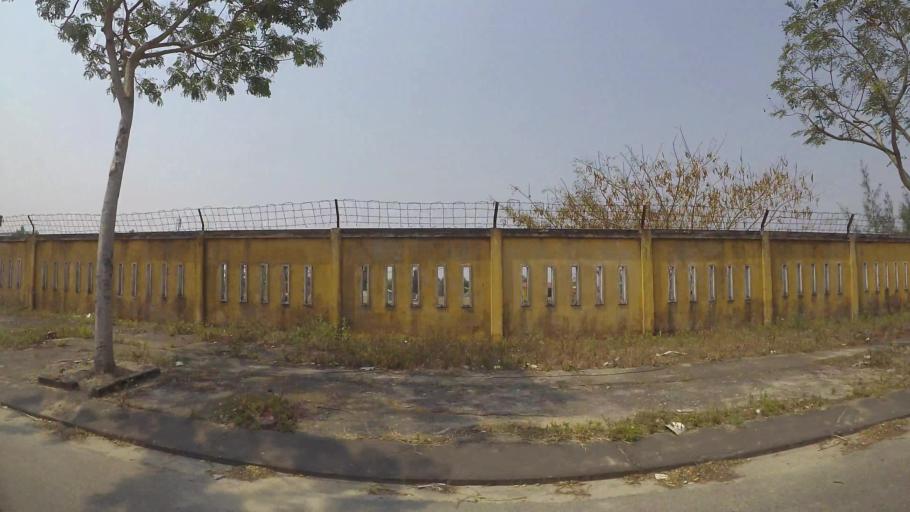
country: VN
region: Da Nang
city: Ngu Hanh Son
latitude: 16.0166
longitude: 108.2509
